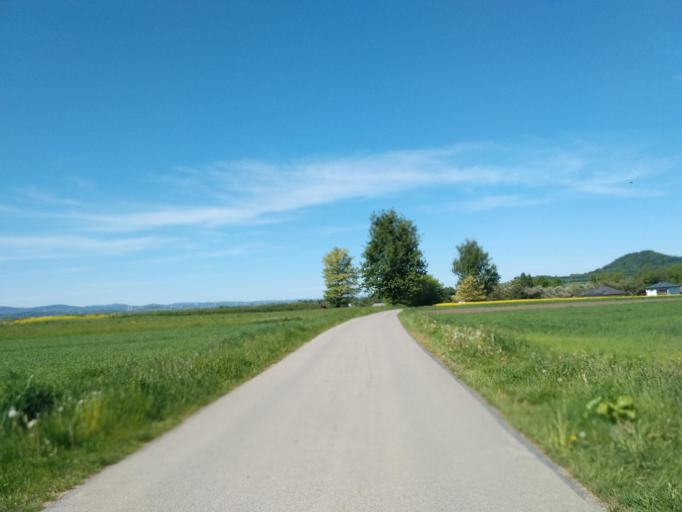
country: PL
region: Subcarpathian Voivodeship
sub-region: Powiat brzozowski
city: Jasionow
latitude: 49.6443
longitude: 21.9895
